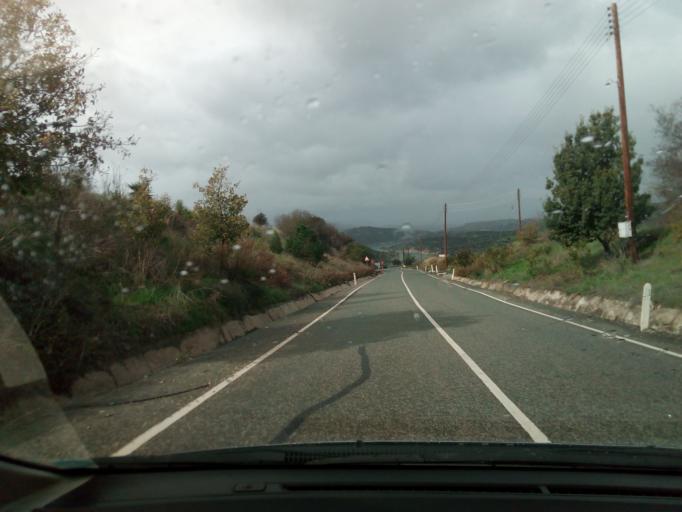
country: CY
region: Pafos
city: Polis
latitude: 34.9476
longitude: 32.4963
